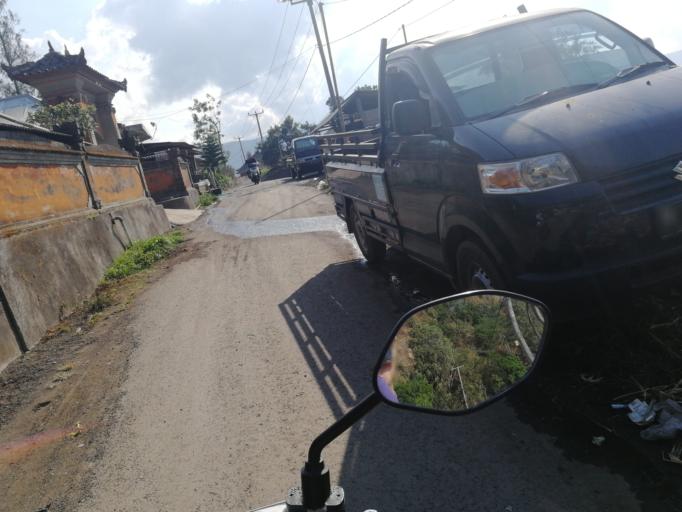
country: ID
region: Bali
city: Banjar Trunyan
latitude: -8.2633
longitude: 115.4221
